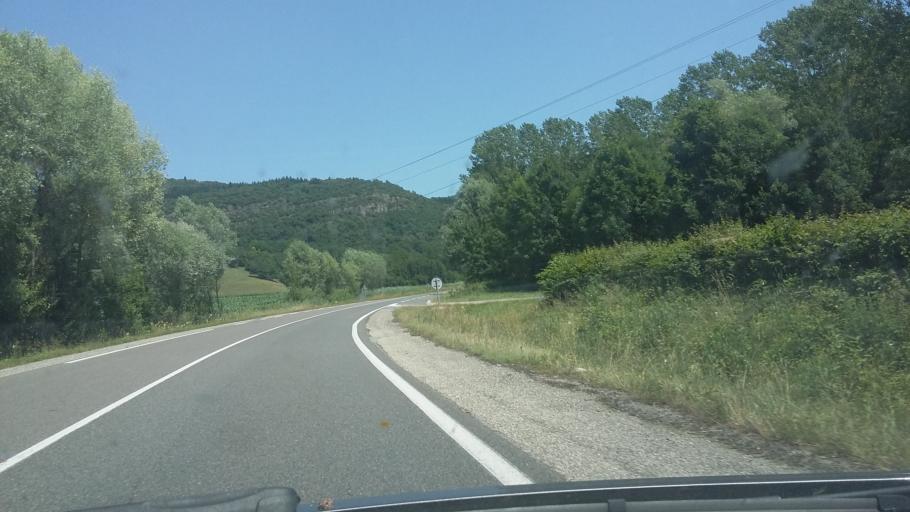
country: FR
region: Rhone-Alpes
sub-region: Departement de l'Ain
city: Belley
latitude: 45.7775
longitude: 5.7003
